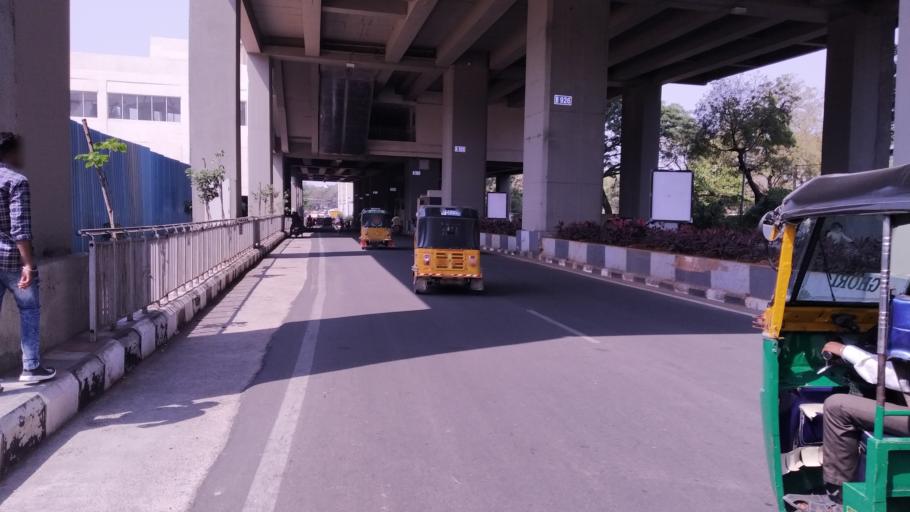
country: IN
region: Telangana
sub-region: Hyderabad
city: Malkajgiri
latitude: 17.4439
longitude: 78.4981
